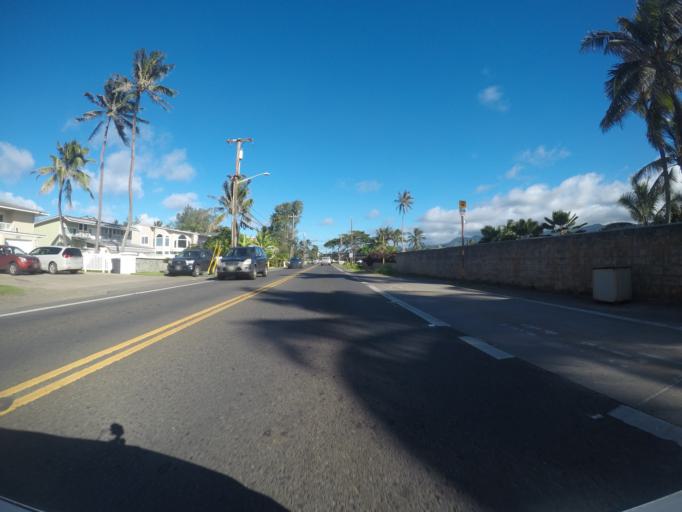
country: US
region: Hawaii
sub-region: Honolulu County
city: La'ie
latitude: 21.6488
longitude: -157.9233
